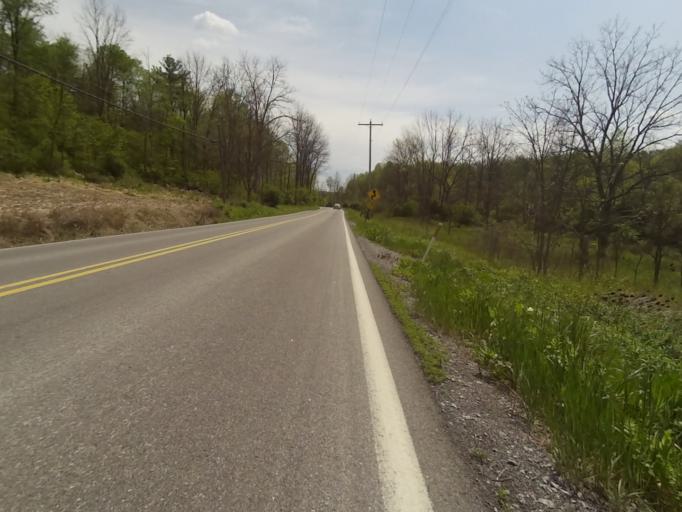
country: US
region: Pennsylvania
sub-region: Centre County
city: Zion
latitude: 40.9918
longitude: -77.6417
